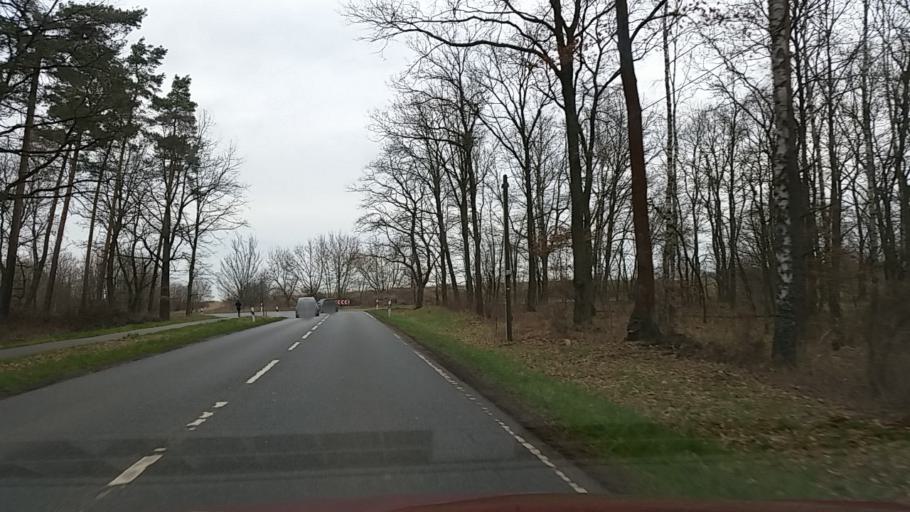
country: DE
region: Lower Saxony
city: Wolfsburg
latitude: 52.4619
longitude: 10.7850
